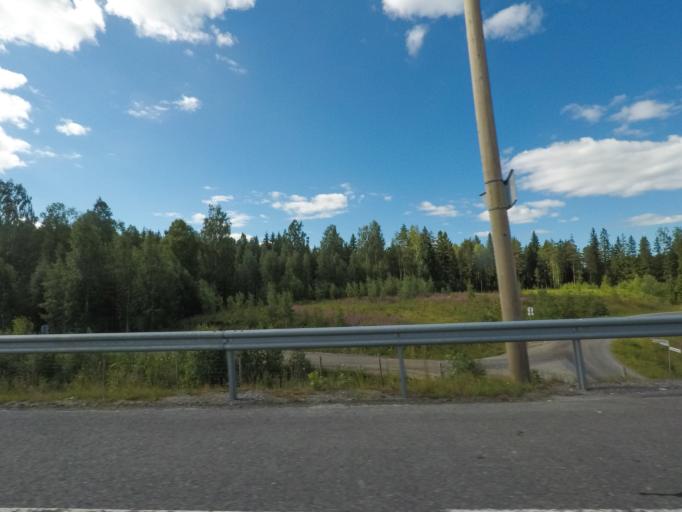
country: FI
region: Southern Savonia
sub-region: Mikkeli
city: Maentyharju
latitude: 61.5375
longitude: 26.8863
